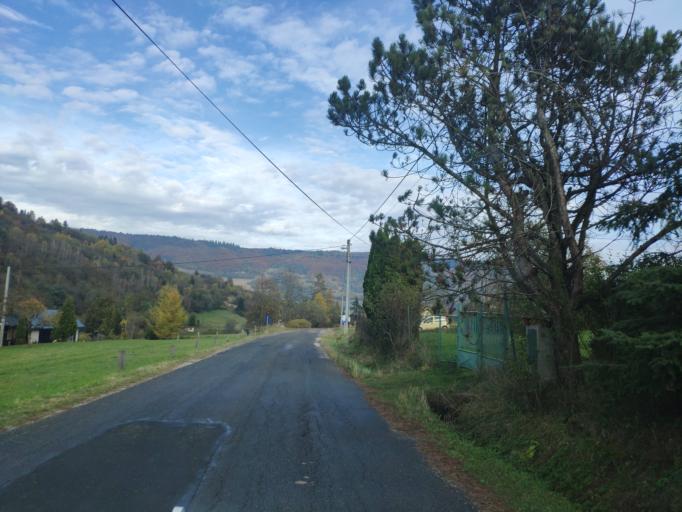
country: SK
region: Kosicky
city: Spisska Nova Ves
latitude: 48.8278
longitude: 20.6282
